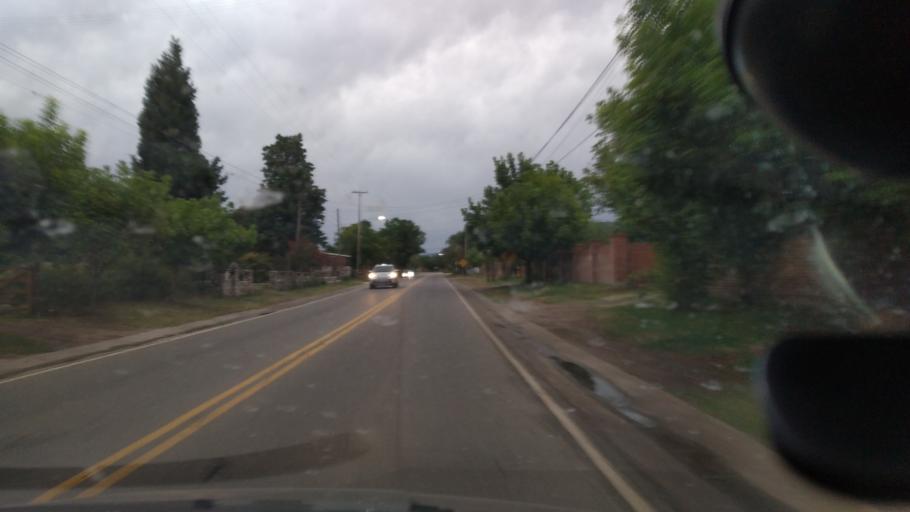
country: AR
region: Cordoba
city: Villa Las Rosas
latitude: -31.9145
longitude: -65.0361
